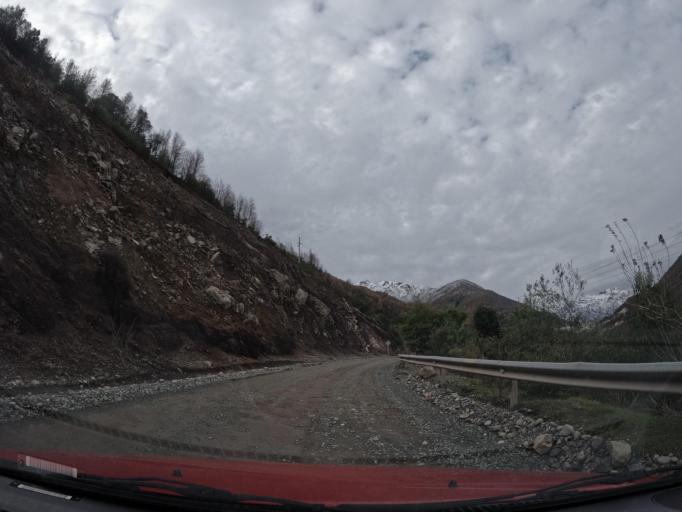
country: CL
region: Maule
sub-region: Provincia de Linares
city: Colbun
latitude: -35.8563
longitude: -71.2076
